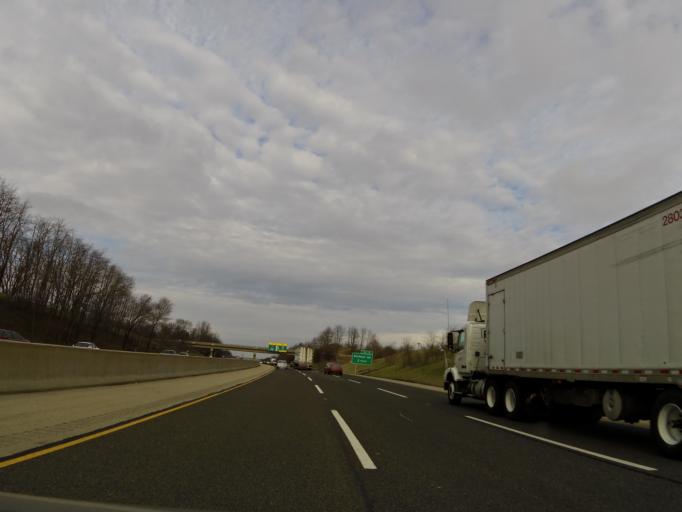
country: US
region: Illinois
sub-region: Winnebago County
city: Roscoe
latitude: 42.4258
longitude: -88.9857
